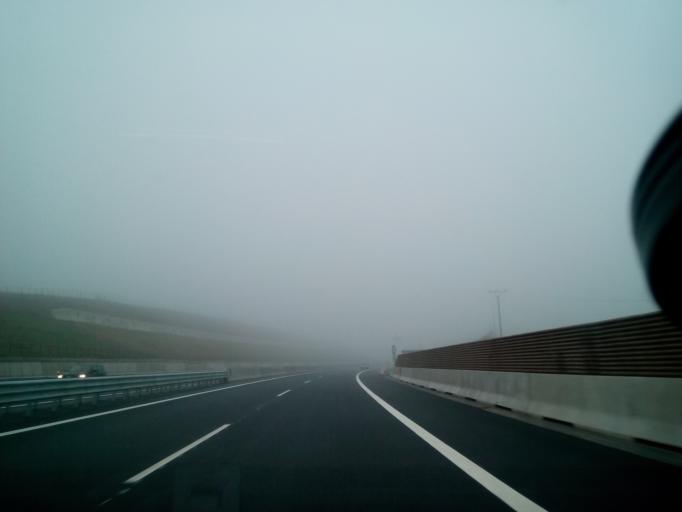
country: SK
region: Presovsky
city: Sabinov
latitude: 49.0260
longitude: 21.0222
